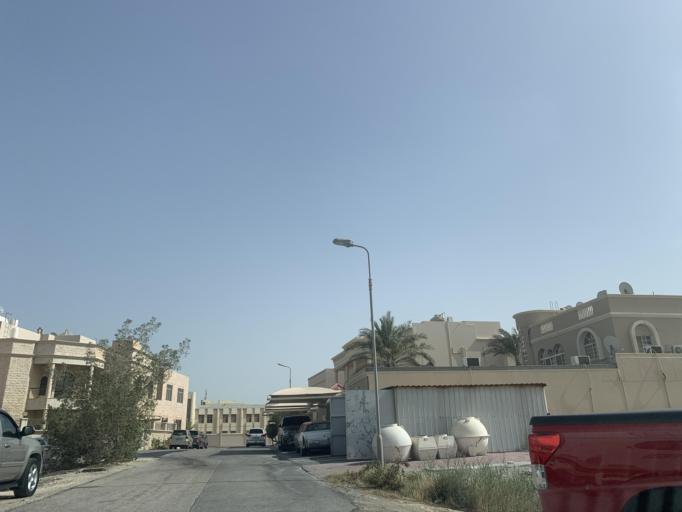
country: BH
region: Northern
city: Ar Rifa'
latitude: 26.1452
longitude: 50.5652
